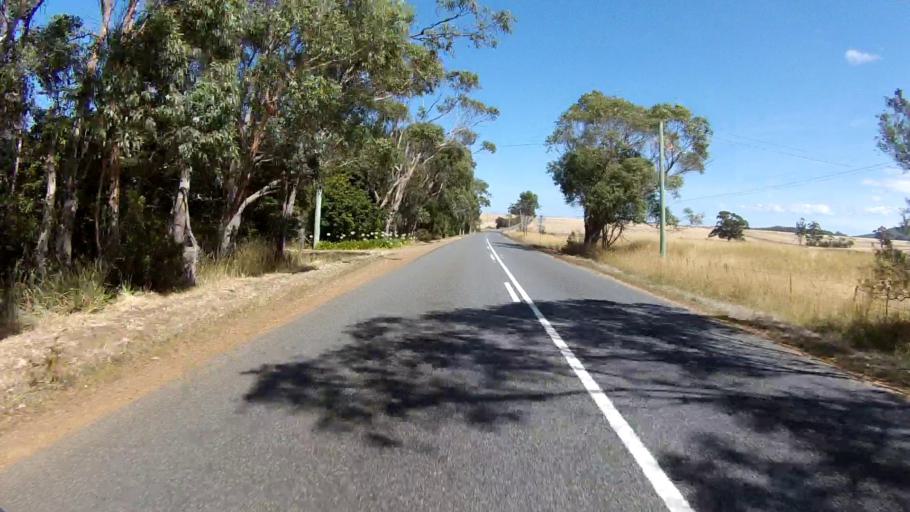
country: AU
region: Tasmania
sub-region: Sorell
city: Sorell
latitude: -42.2440
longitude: 148.0112
